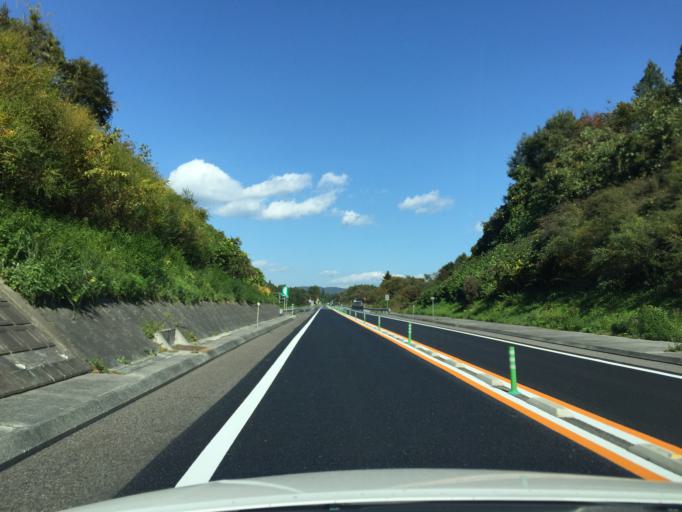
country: JP
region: Fukushima
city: Funehikimachi-funehiki
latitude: 37.2820
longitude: 140.6011
